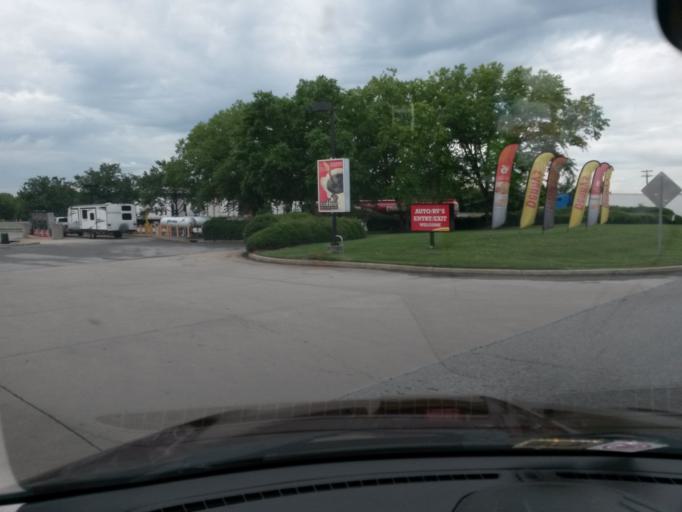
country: US
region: South Carolina
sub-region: Cherokee County
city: Blacksburg
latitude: 35.1421
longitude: -81.5084
